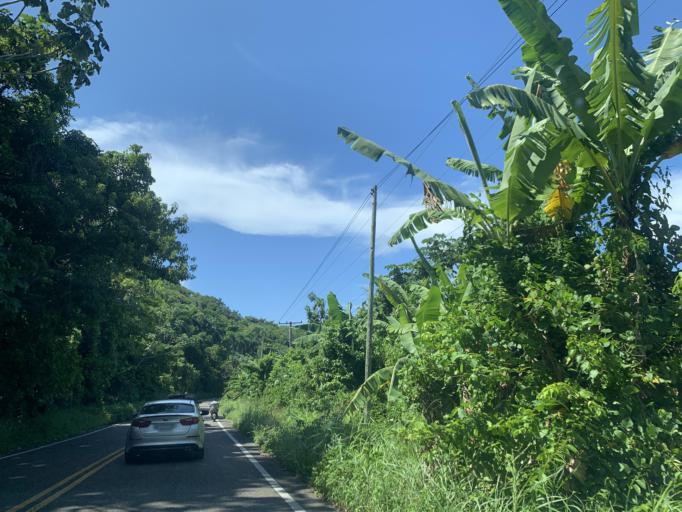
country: DO
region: Maria Trinidad Sanchez
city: Cabrera
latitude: 19.6569
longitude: -69.9370
